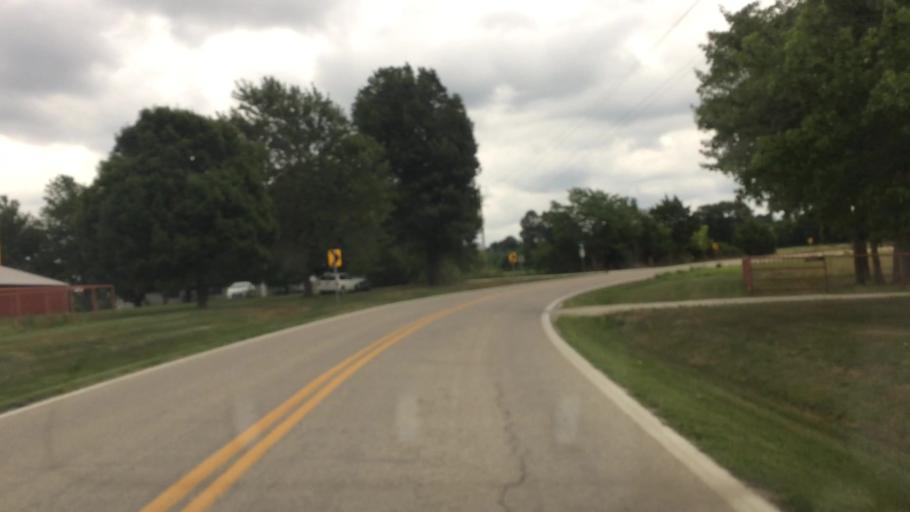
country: US
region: Missouri
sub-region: Greene County
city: Strafford
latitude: 37.2997
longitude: -93.1228
